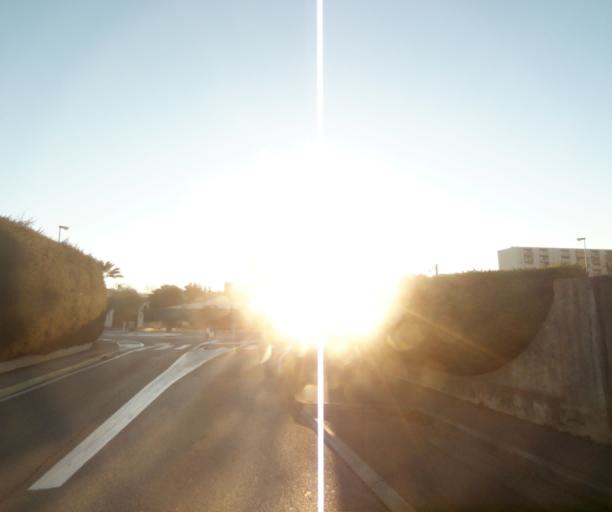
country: FR
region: Provence-Alpes-Cote d'Azur
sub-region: Departement des Alpes-Maritimes
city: Vallauris
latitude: 43.5789
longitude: 7.0883
